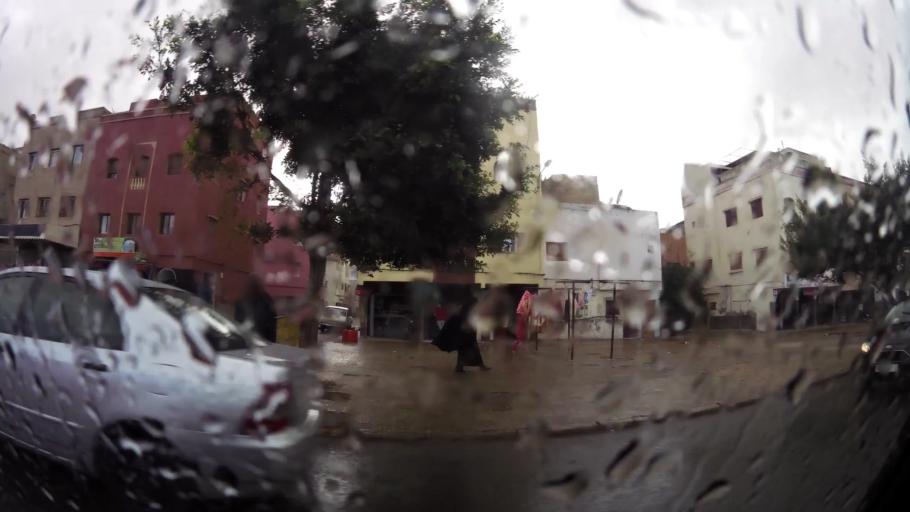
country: MA
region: Grand Casablanca
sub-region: Casablanca
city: Casablanca
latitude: 33.5584
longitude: -7.6895
